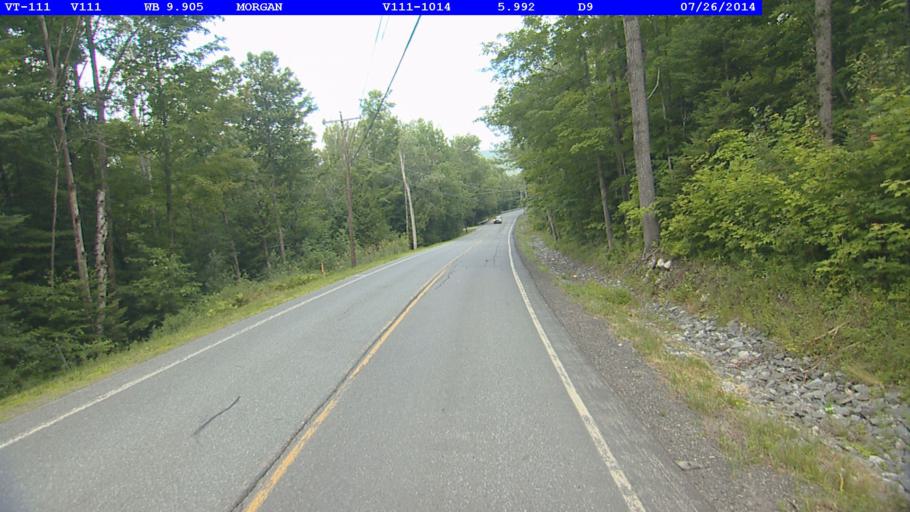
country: US
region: Vermont
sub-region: Orleans County
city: Newport
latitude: 44.8951
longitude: -71.9719
